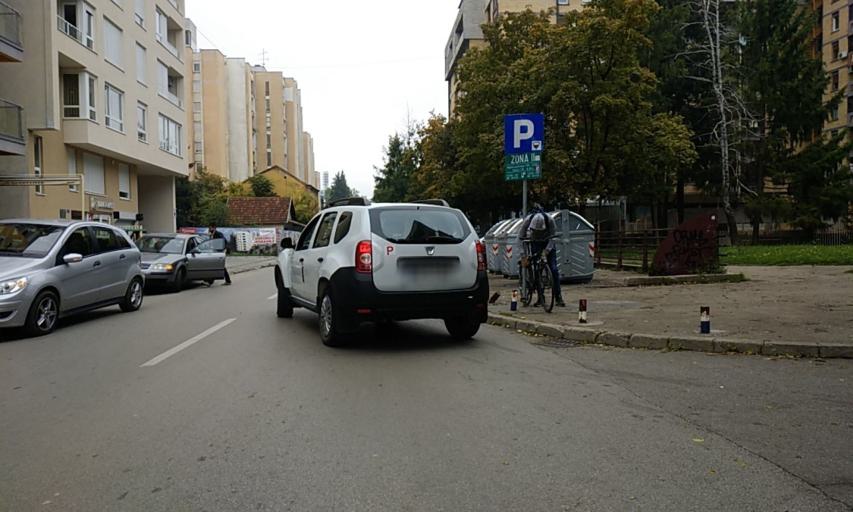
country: BA
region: Republika Srpska
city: Mejdan - Obilicevo
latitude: 44.7714
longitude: 17.1972
